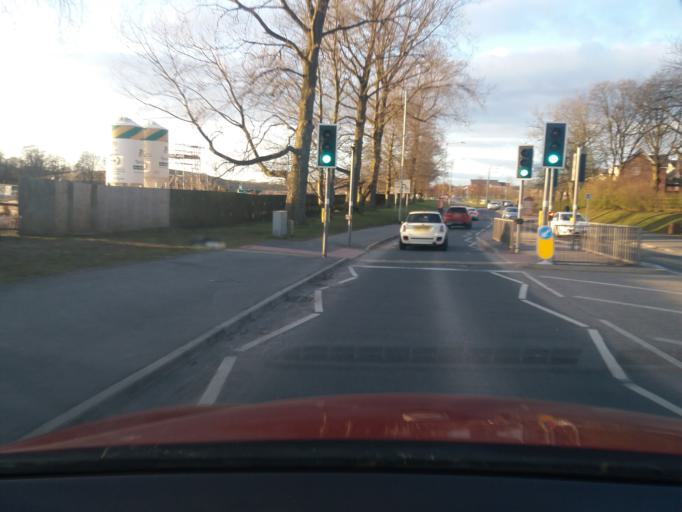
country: GB
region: England
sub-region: Lancashire
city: Euxton
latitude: 53.6754
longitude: -2.6637
